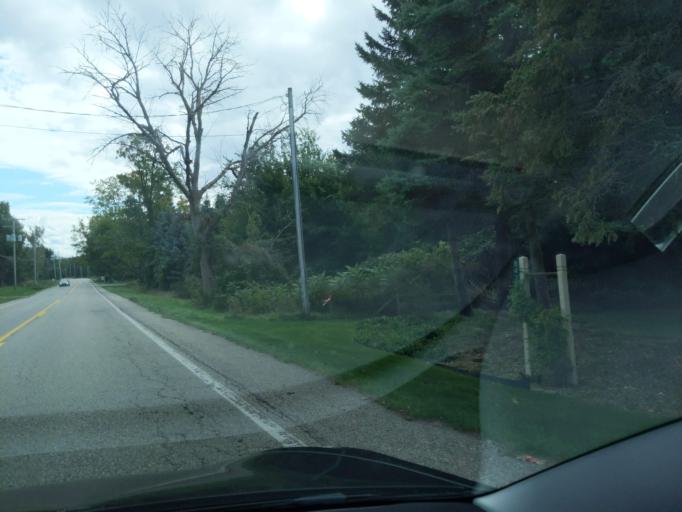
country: US
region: Michigan
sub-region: Kalkaska County
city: Rapid City
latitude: 44.9116
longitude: -85.2835
